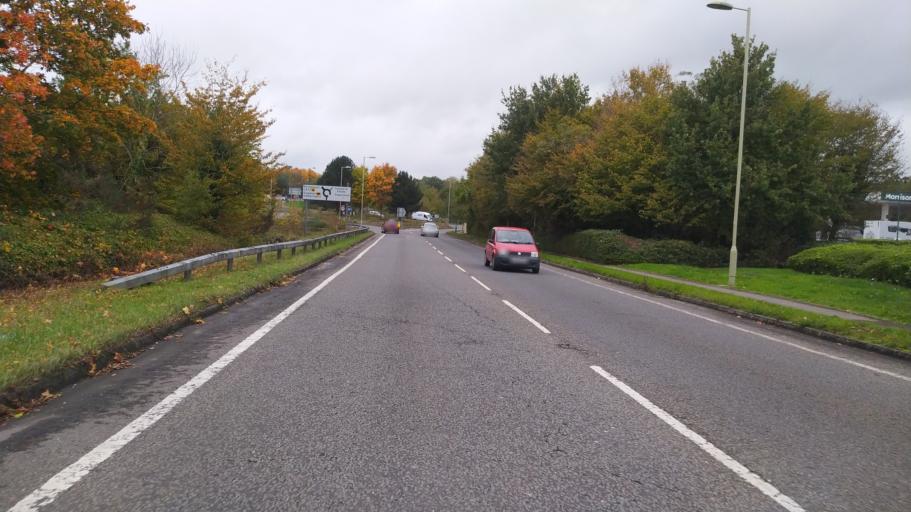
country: GB
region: England
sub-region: Hampshire
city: Cowplain
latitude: 50.9073
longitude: -1.0030
